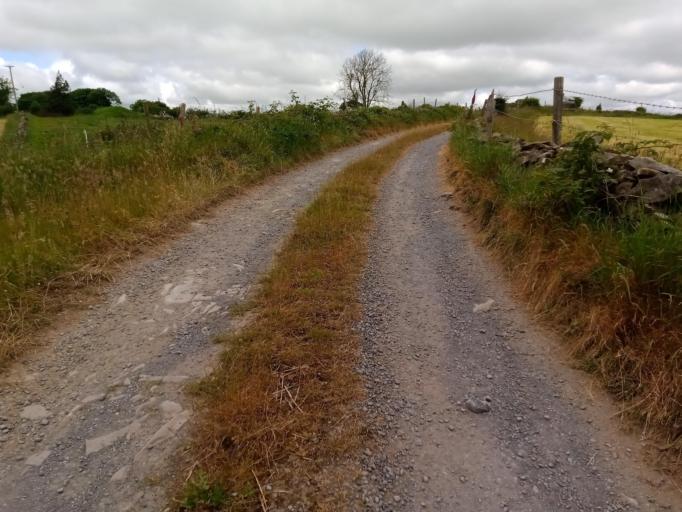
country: IE
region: Leinster
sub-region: Laois
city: Rathdowney
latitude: 52.7959
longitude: -7.4644
